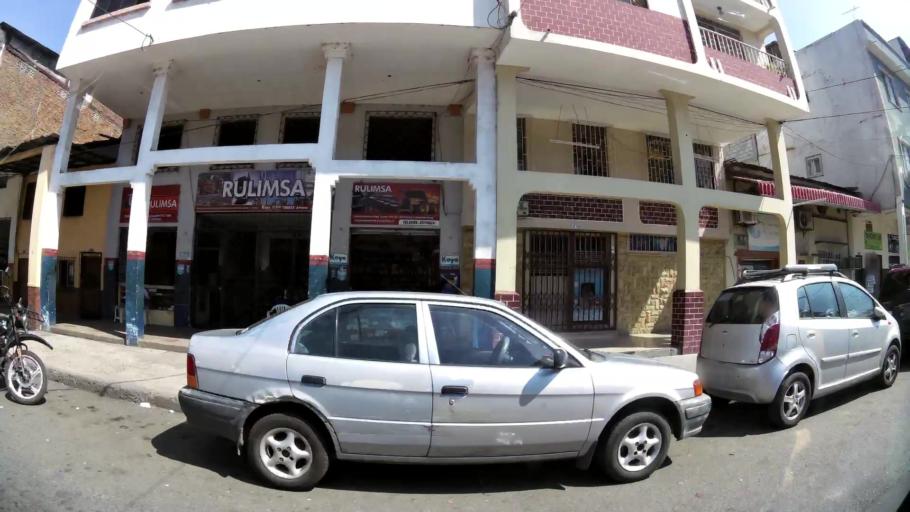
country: EC
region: Guayas
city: Guayaquil
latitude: -2.1918
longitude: -79.8923
